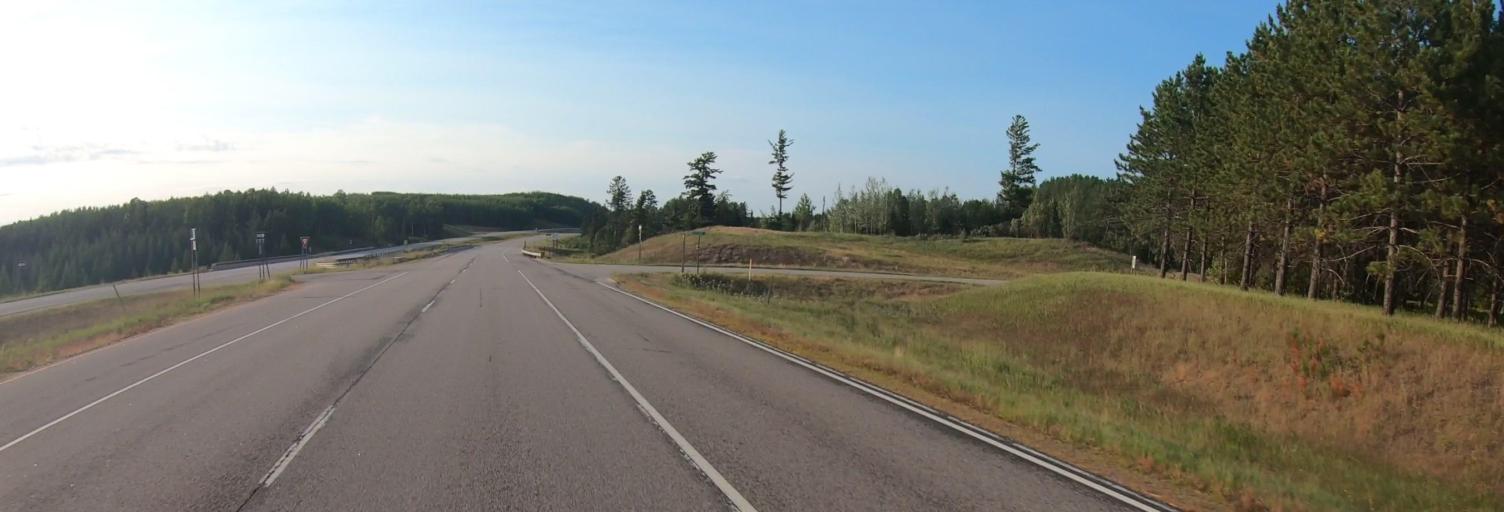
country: US
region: Minnesota
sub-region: Saint Louis County
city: Mountain Iron
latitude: 47.6770
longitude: -92.6351
